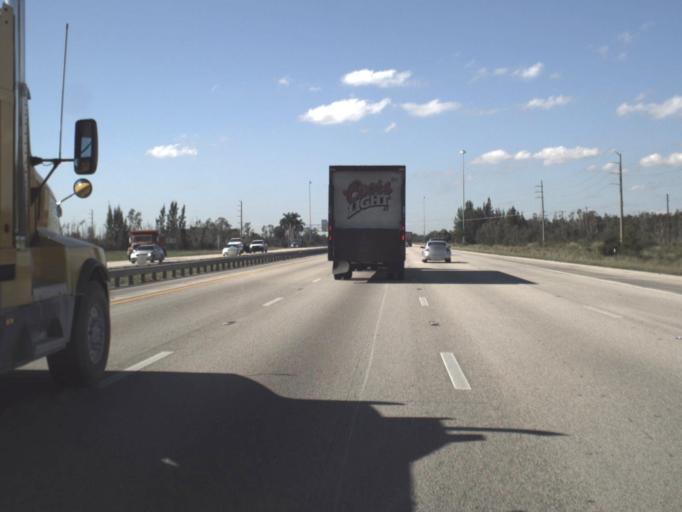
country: US
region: Florida
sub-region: Miami-Dade County
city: Palm Springs North
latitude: 25.9460
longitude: -80.3549
